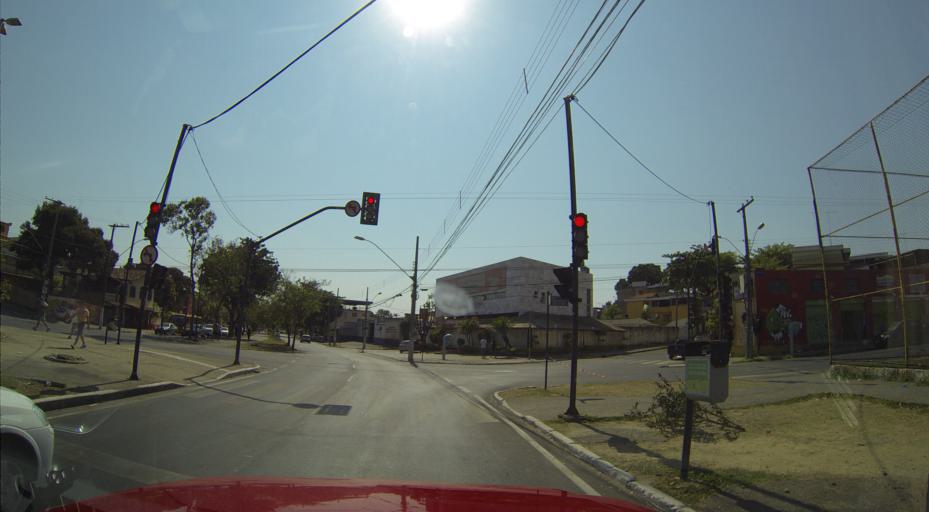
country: BR
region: Minas Gerais
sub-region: Belo Horizonte
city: Belo Horizonte
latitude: -19.8870
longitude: -43.9447
